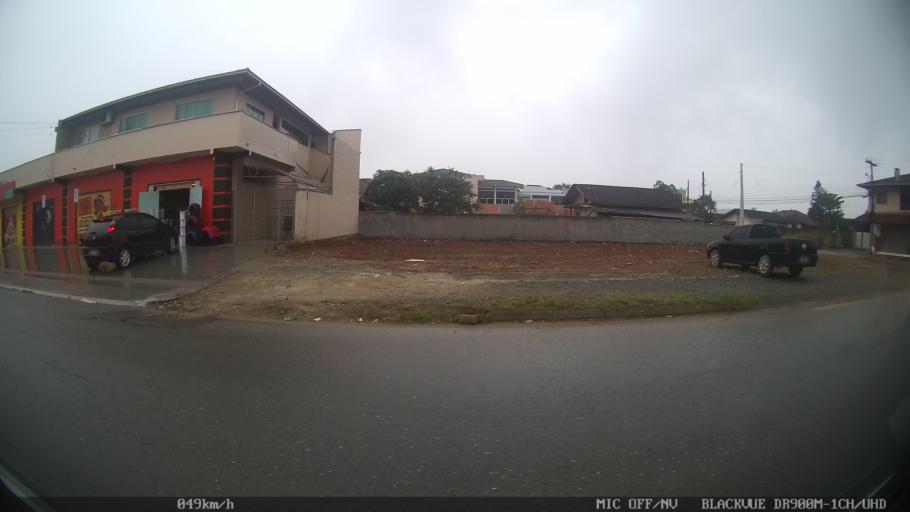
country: BR
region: Santa Catarina
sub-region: Joinville
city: Joinville
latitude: -26.2098
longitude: -48.8264
